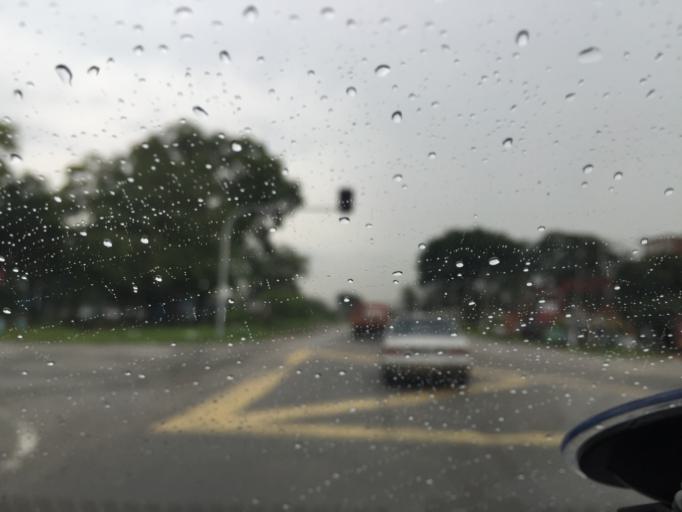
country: MY
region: Selangor
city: Subang Jaya
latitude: 3.0108
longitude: 101.5184
